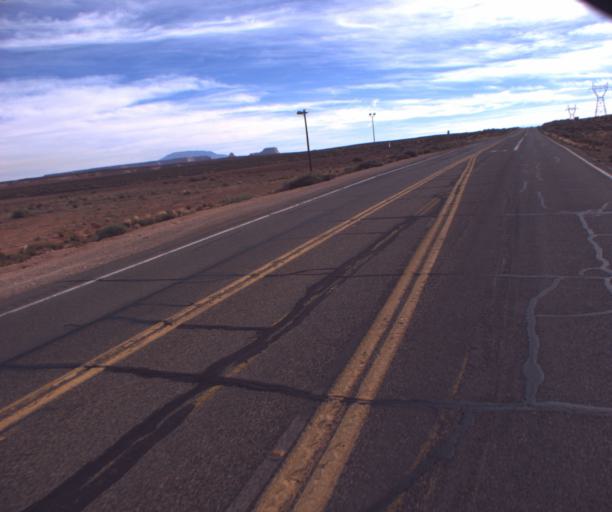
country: US
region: Arizona
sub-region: Coconino County
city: LeChee
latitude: 36.8937
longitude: -111.3842
